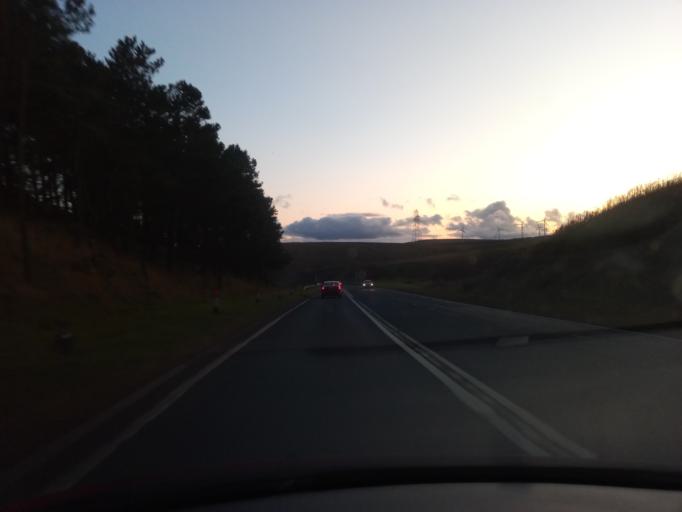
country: GB
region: Scotland
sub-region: East Lothian
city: Pencaitland
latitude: 55.8033
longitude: -2.8360
